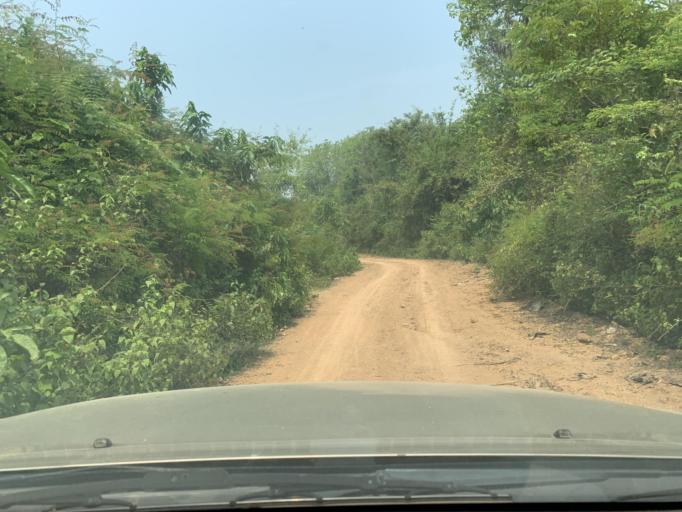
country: LA
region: Louangphabang
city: Louangphabang
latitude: 19.9632
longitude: 102.1271
